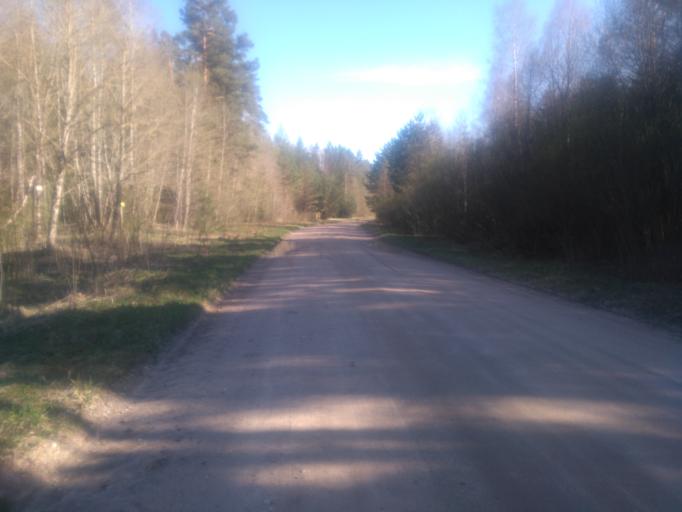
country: LV
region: Vecpiebalga
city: Vecpiebalga
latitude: 57.0121
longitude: 25.8392
